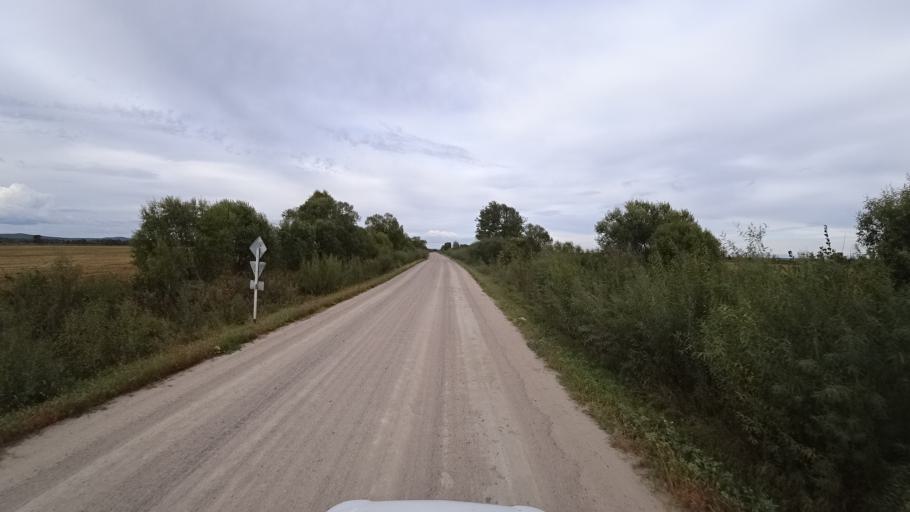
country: RU
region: Amur
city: Arkhara
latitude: 49.3724
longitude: 130.1456
